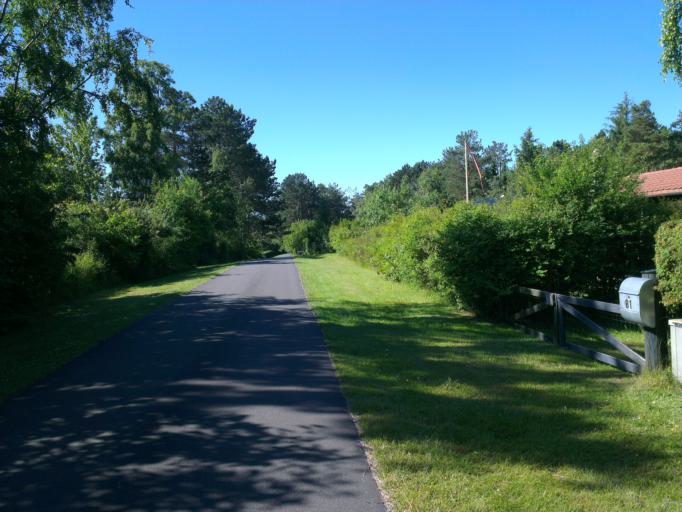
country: DK
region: Capital Region
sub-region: Halsnaes Kommune
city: Hundested
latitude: 55.9275
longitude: 11.9075
